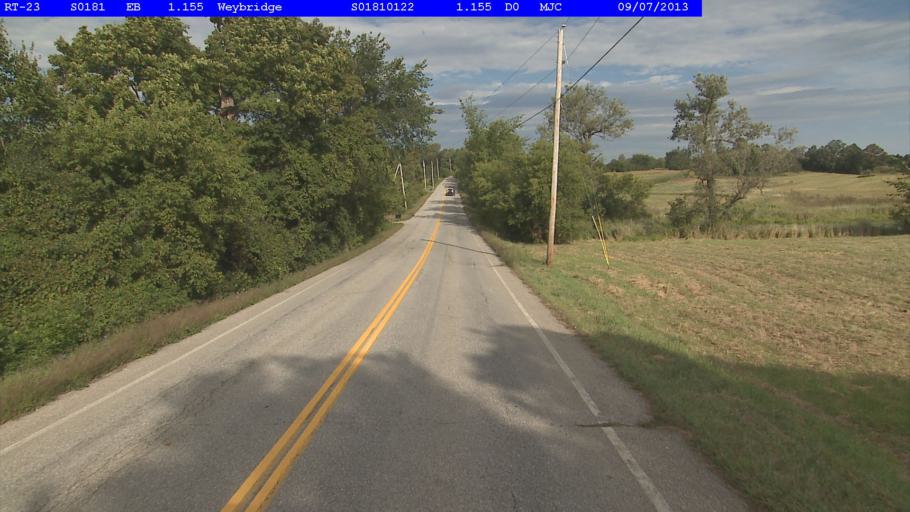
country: US
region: Vermont
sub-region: Addison County
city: Middlebury (village)
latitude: 44.0295
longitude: -73.2002
